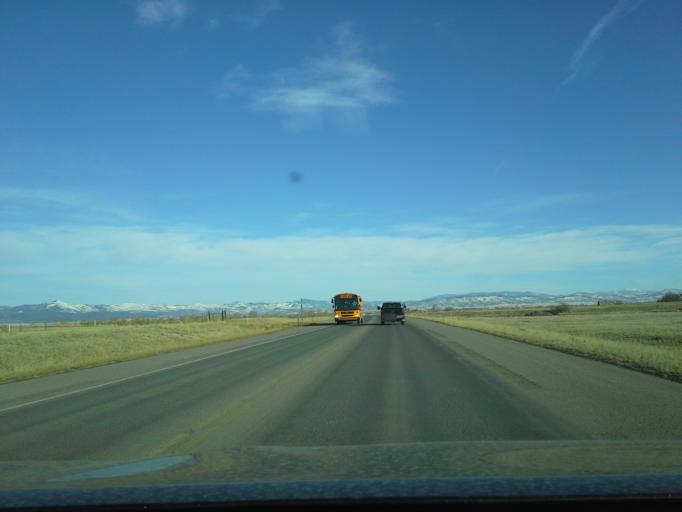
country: US
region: Montana
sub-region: Lewis and Clark County
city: Helena
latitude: 46.6163
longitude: -111.9827
